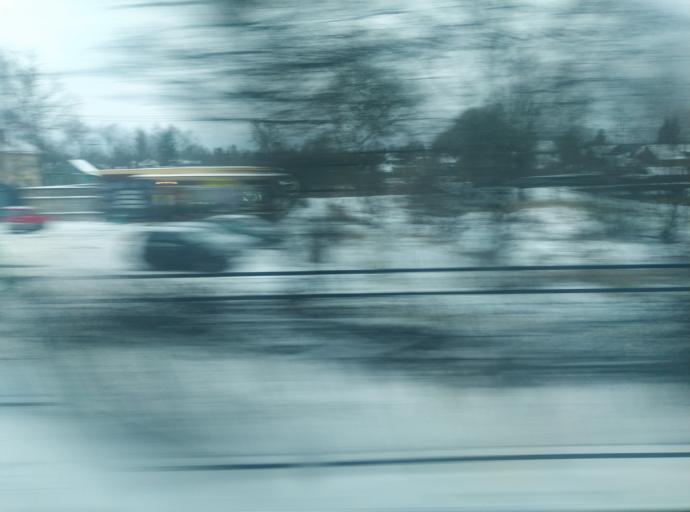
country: RU
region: Leningrad
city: Ul'yanovka
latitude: 59.6357
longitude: 30.7562
